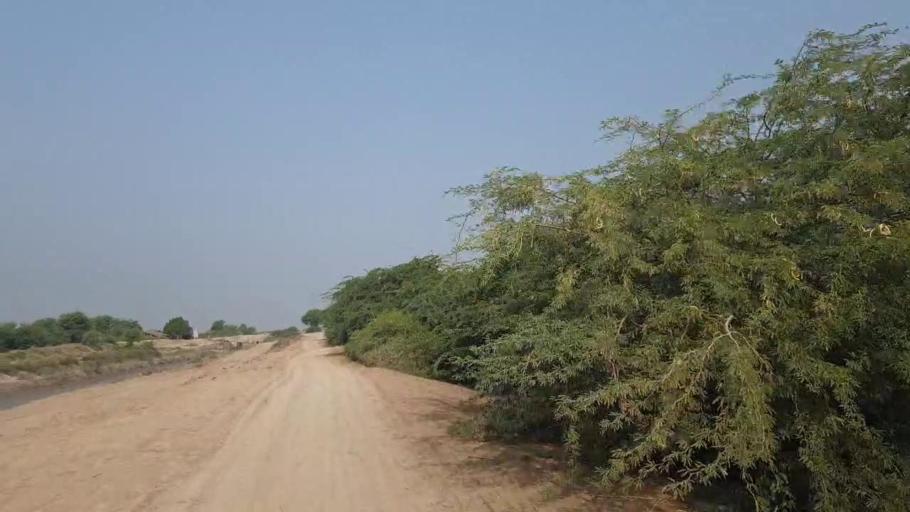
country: PK
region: Sindh
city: Badin
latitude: 24.7043
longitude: 68.7759
